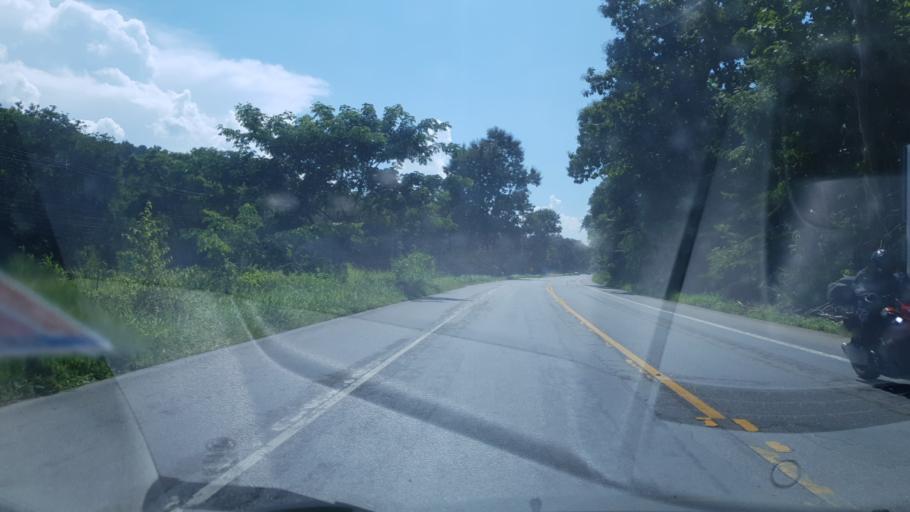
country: TH
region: Chiang Rai
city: Mae Suai
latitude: 19.6940
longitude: 99.5785
